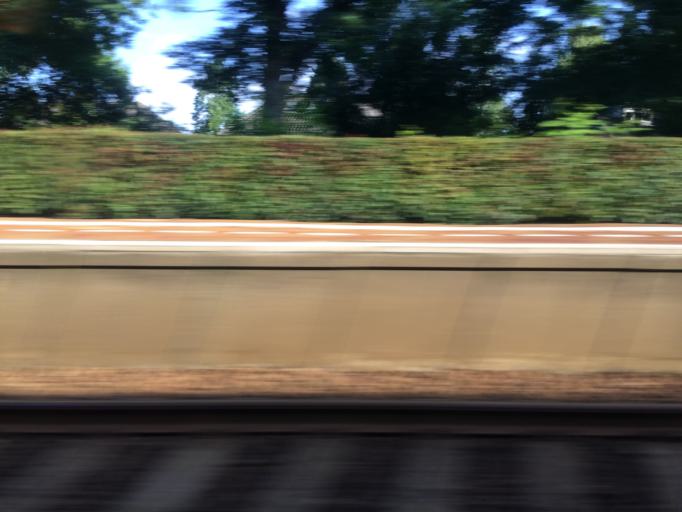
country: NL
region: North Brabant
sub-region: Gemeente 's-Hertogenbosch
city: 's-Hertogenbosch
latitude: 51.7145
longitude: 5.3672
